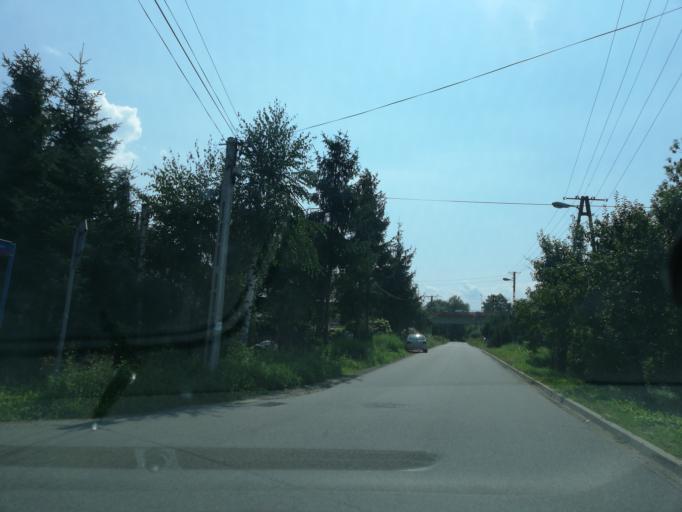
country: PL
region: Lesser Poland Voivodeship
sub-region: Powiat nowosadecki
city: Chelmiec
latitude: 49.6434
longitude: 20.6756
